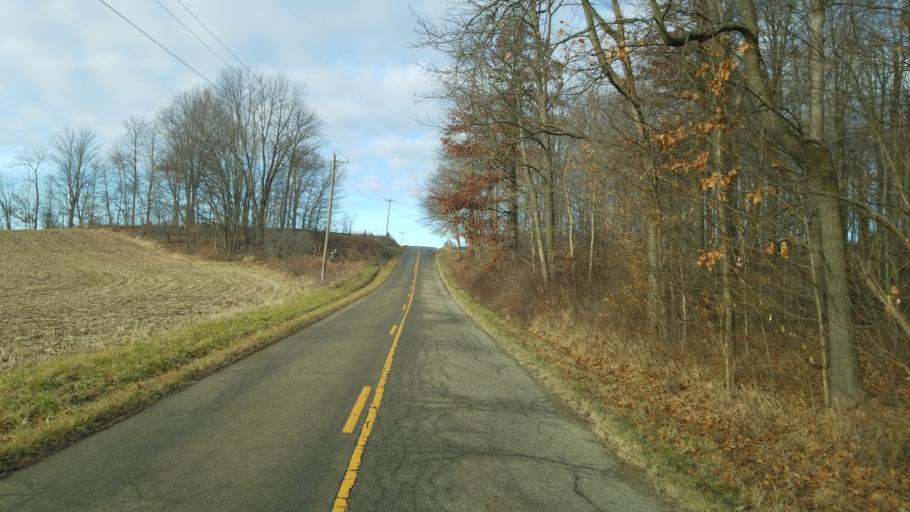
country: US
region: Ohio
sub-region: Knox County
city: Gambier
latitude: 40.3135
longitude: -82.3294
